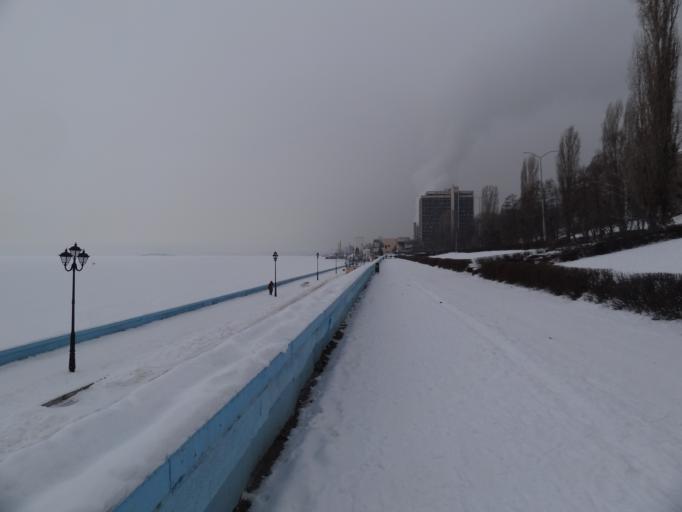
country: RU
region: Saratov
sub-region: Saratovskiy Rayon
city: Saratov
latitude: 51.5237
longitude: 46.0433
